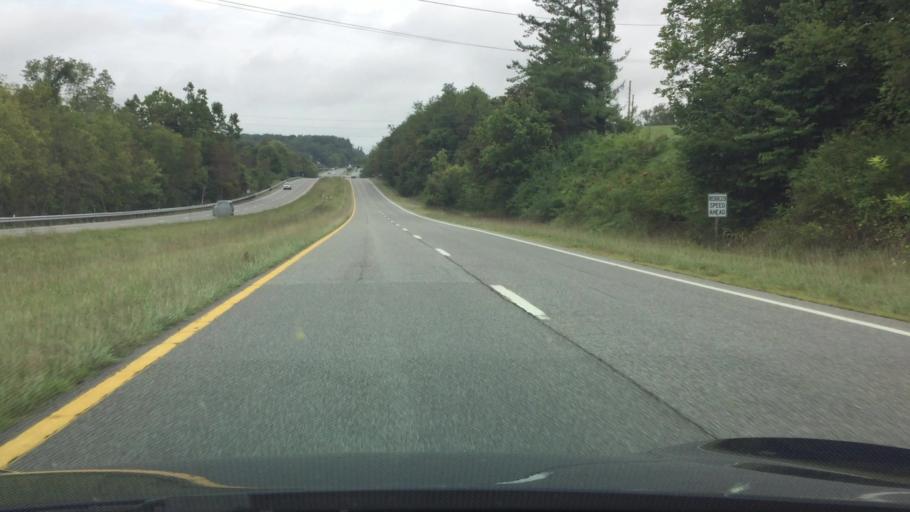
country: US
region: Virginia
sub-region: City of Radford
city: Radford
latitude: 37.1136
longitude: -80.5261
